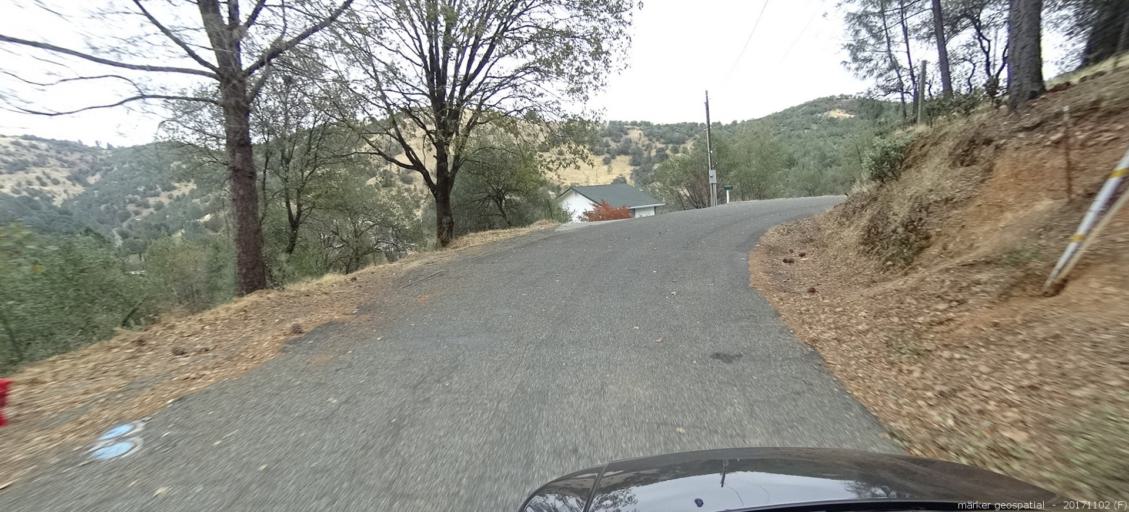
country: US
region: California
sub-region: Shasta County
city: Bella Vista
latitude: 40.7167
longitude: -122.2371
